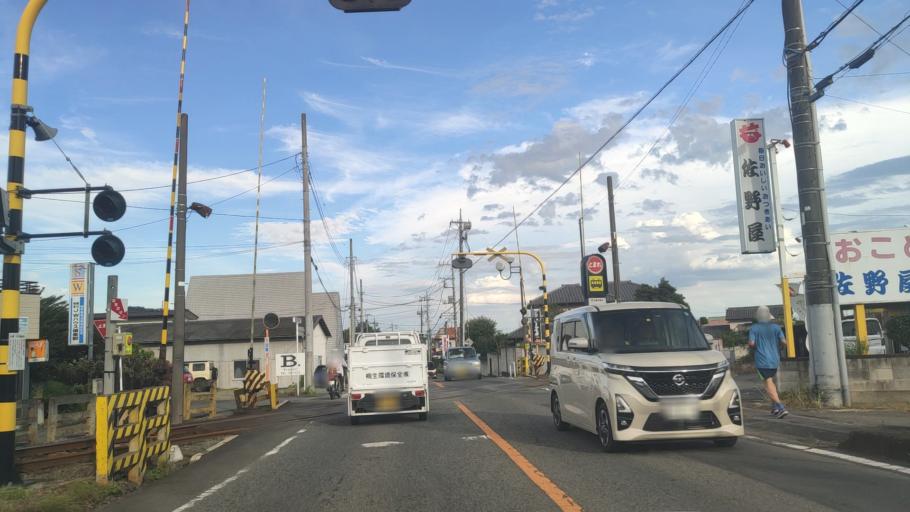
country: JP
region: Gunma
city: Omamacho-omama
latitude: 36.4237
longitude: 139.2998
